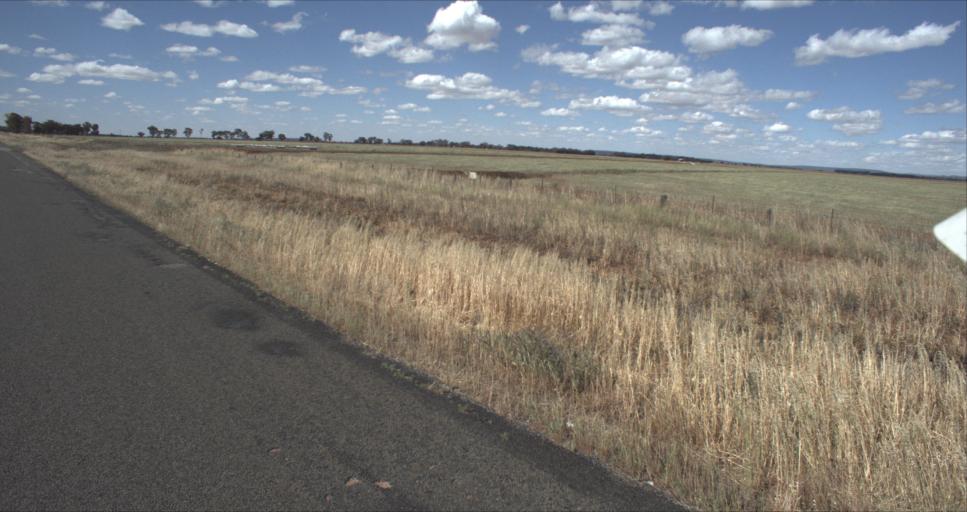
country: AU
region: New South Wales
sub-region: Leeton
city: Leeton
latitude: -34.4662
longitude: 146.2518
